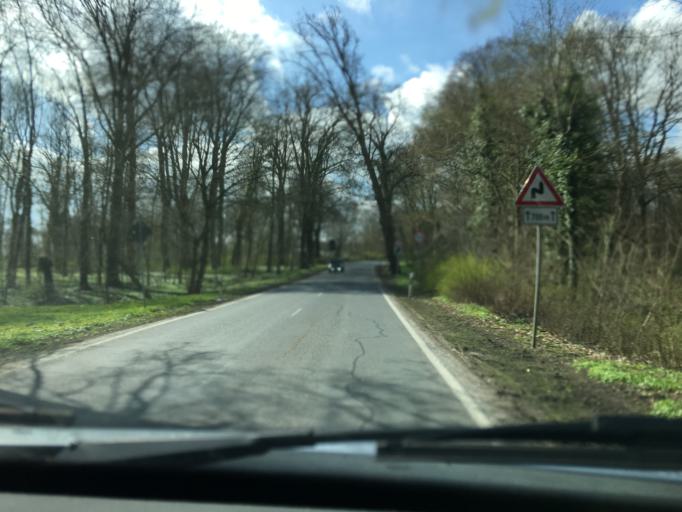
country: DE
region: Mecklenburg-Vorpommern
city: Bad Sulze
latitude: 54.1779
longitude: 12.6572
